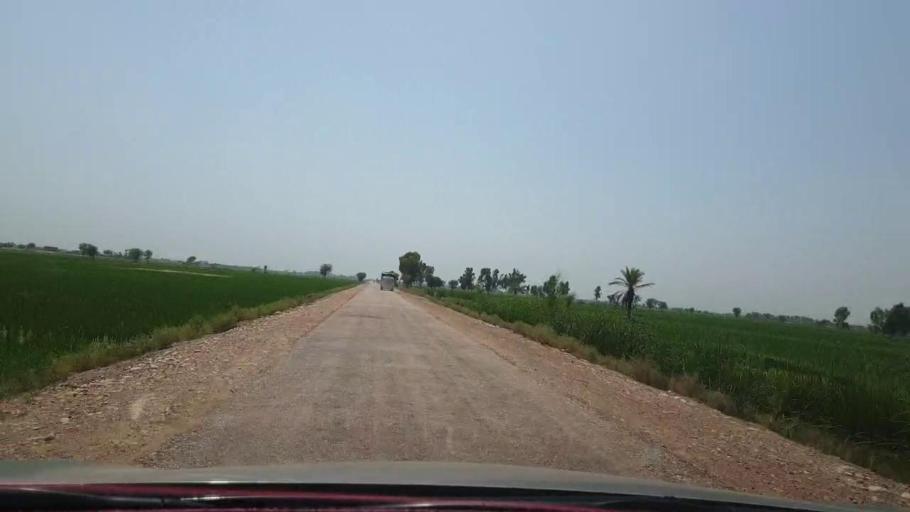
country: PK
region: Sindh
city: Warah
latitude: 27.5617
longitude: 67.8006
